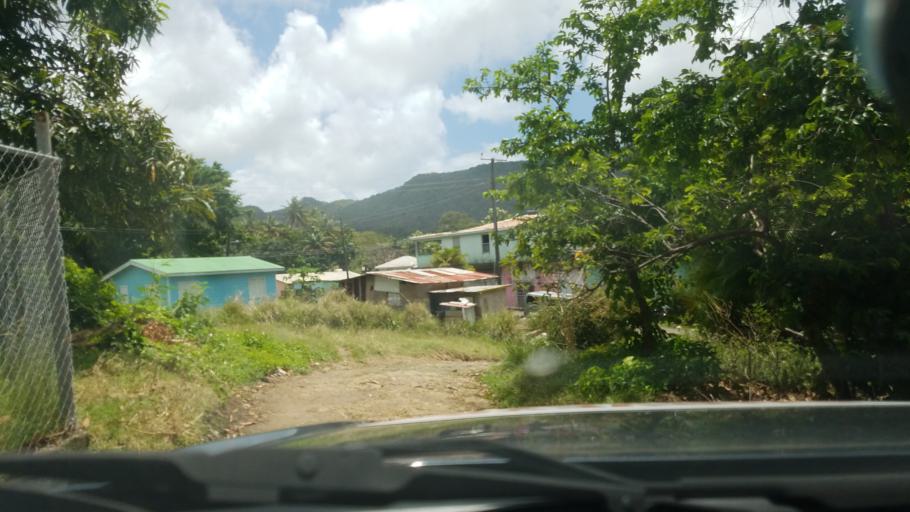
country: LC
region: Gros-Islet
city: Gros Islet
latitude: 14.0539
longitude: -60.9296
